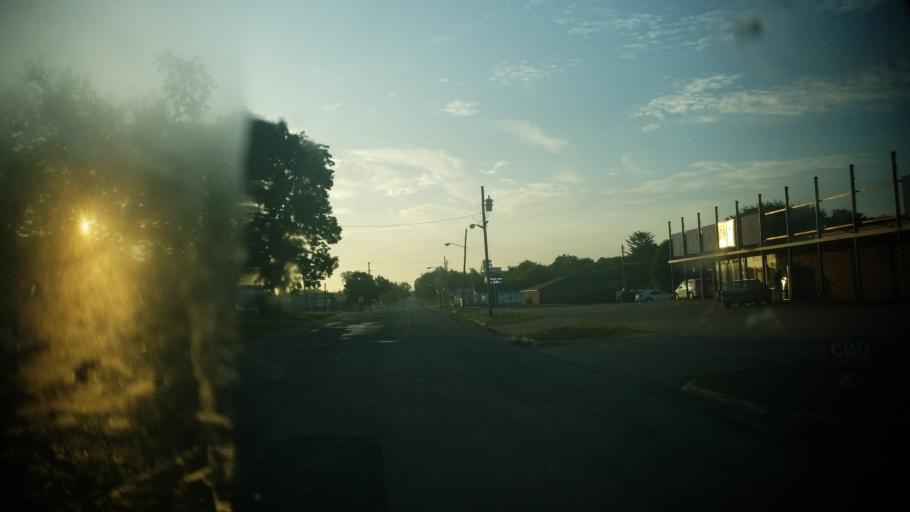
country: US
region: Illinois
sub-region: Wayne County
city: Fairfield
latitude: 38.3787
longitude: -88.3681
